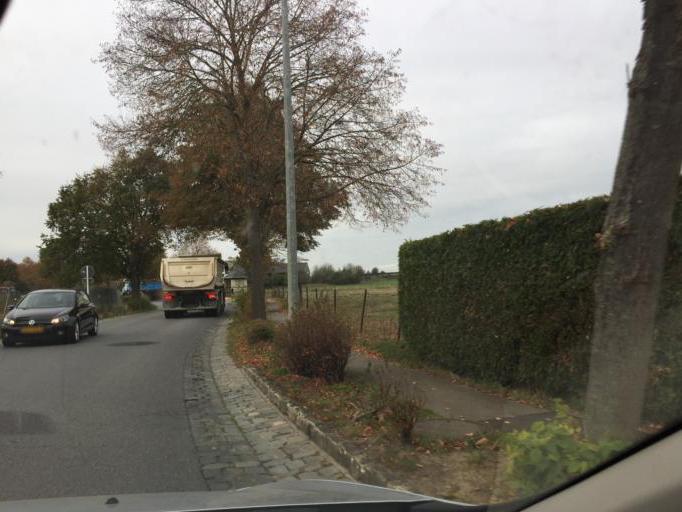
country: LU
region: Luxembourg
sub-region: Canton de Capellen
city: Kehlen
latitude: 49.6680
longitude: 6.0301
